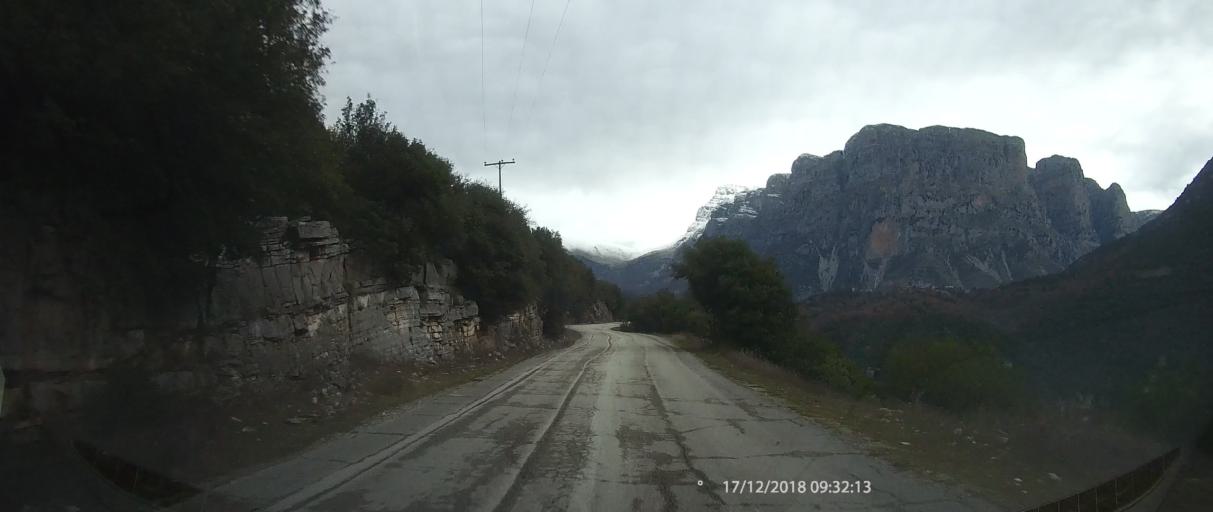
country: GR
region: Epirus
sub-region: Nomos Ioanninon
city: Kalpaki
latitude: 39.9514
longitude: 20.6913
